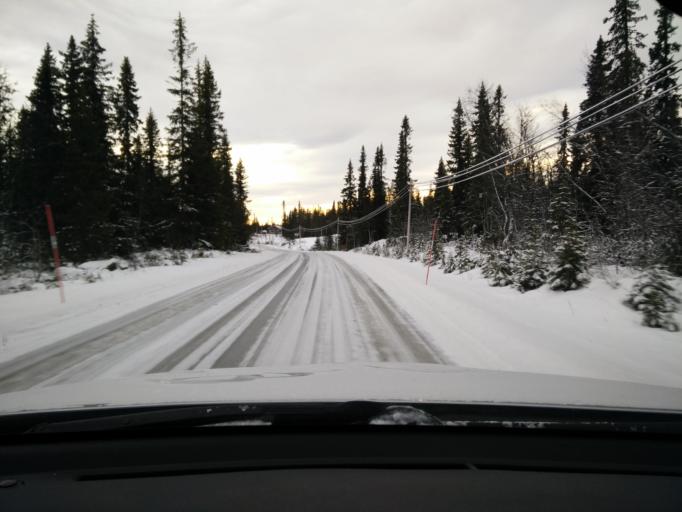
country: SE
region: Jaemtland
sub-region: Bergs Kommun
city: Hoverberg
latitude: 62.4827
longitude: 14.1217
